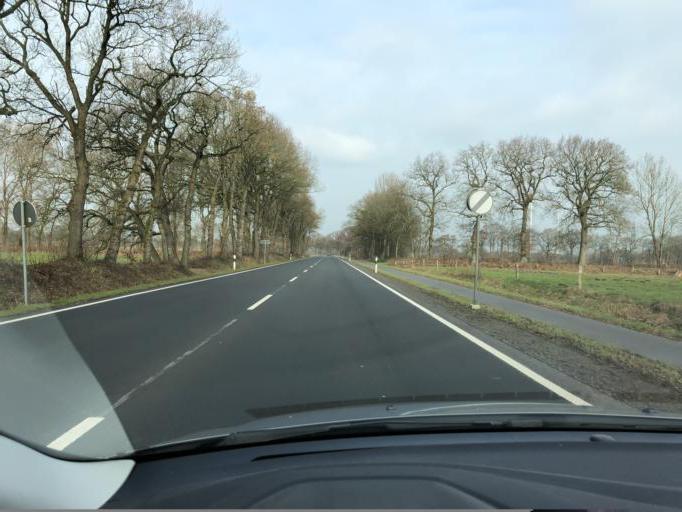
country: DE
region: Lower Saxony
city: Mittegrossefehn
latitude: 53.3546
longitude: 7.6005
